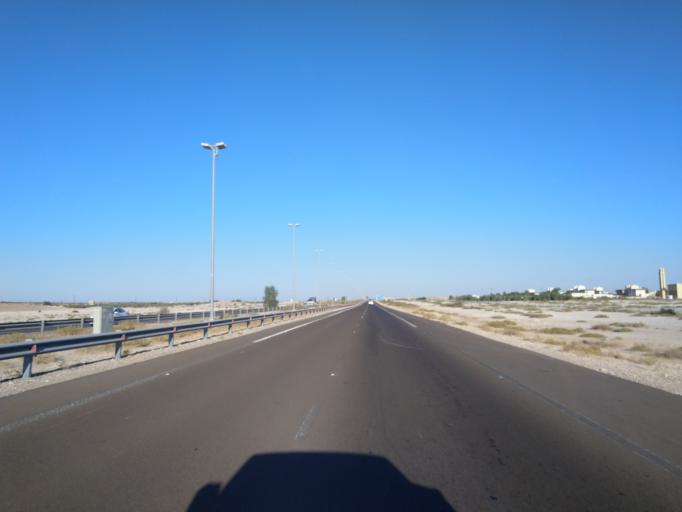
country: OM
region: Al Buraimi
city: Al Buraymi
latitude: 24.5232
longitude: 55.5382
